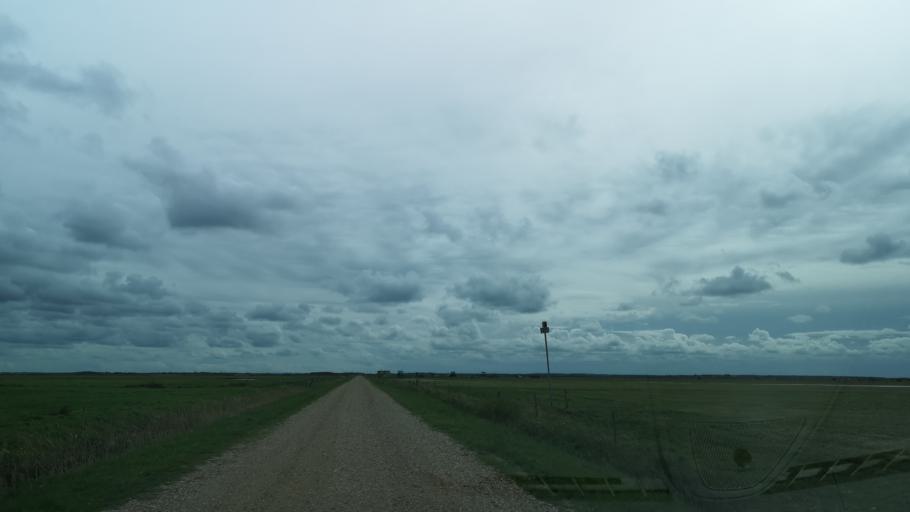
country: DK
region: Central Jutland
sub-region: Ringkobing-Skjern Kommune
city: Hvide Sande
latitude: 55.8802
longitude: 8.2232
